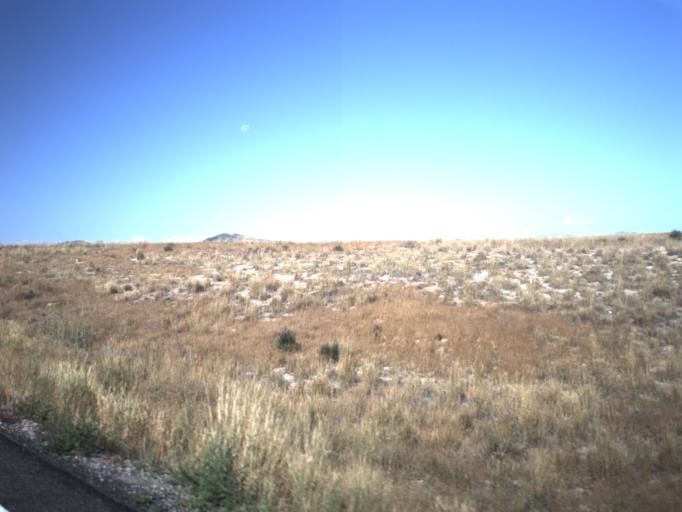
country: US
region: Utah
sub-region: Juab County
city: Mona
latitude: 39.7058
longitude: -112.2118
